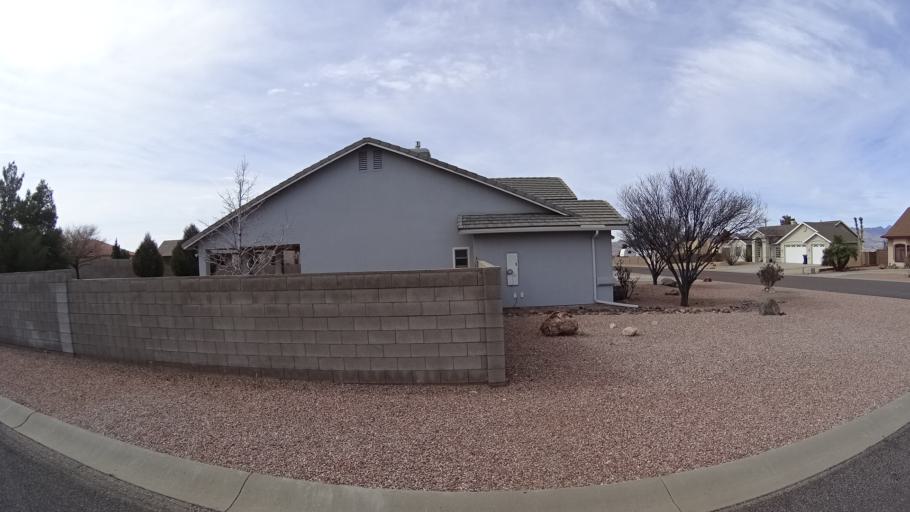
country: US
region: Arizona
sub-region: Mohave County
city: Kingman
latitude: 35.1950
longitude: -113.9832
